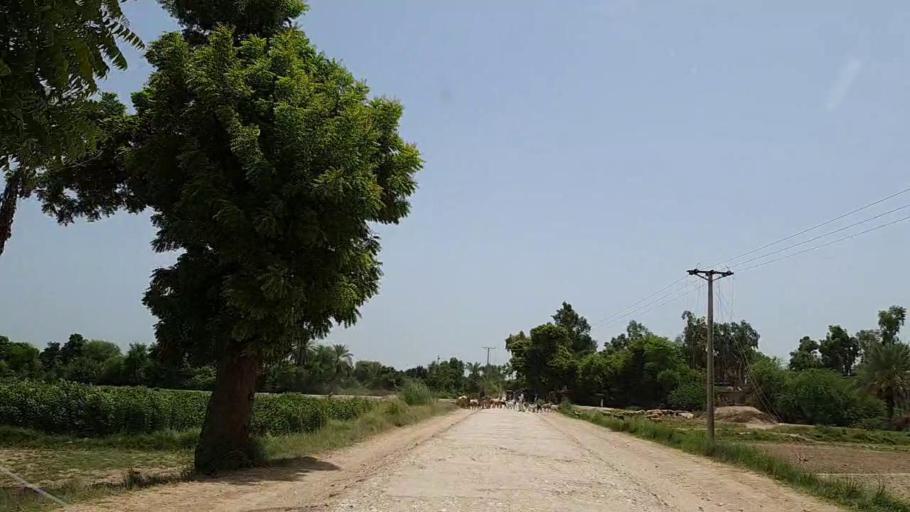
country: PK
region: Sindh
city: Tharu Shah
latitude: 26.9475
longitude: 68.1032
